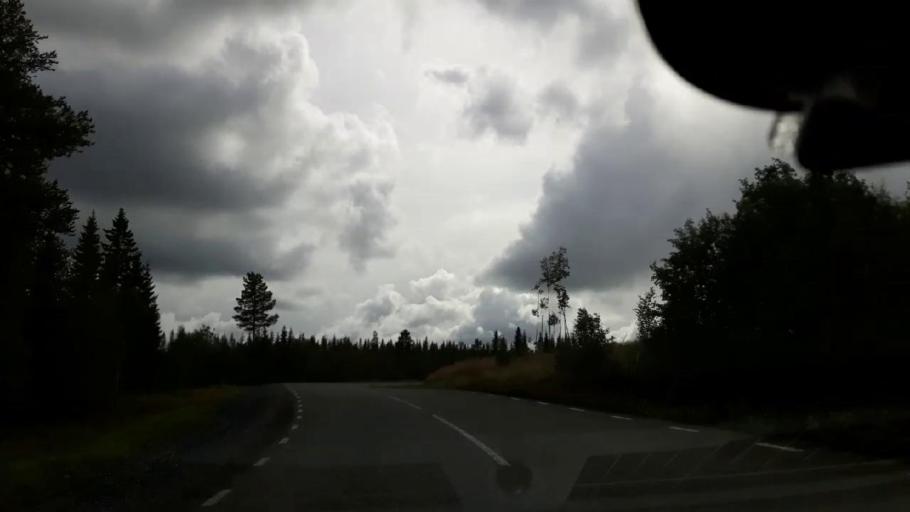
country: SE
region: Jaemtland
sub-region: Krokoms Kommun
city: Valla
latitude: 63.4750
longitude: 13.8466
